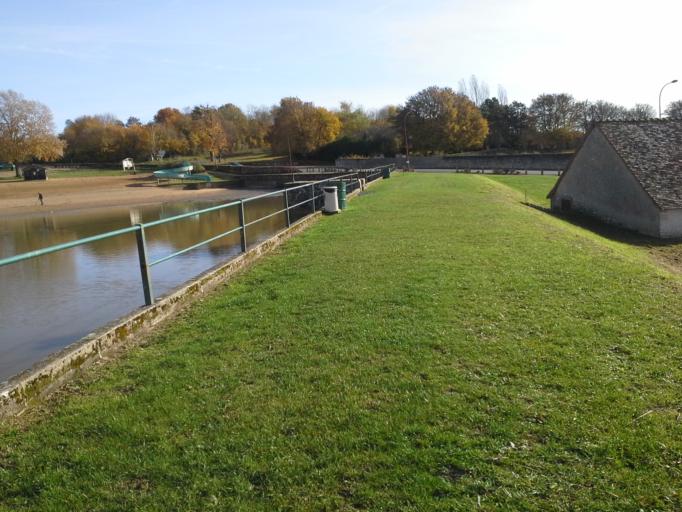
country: FR
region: Poitou-Charentes
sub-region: Departement de la Vienne
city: Pleumartin
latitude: 46.6434
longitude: 0.7552
